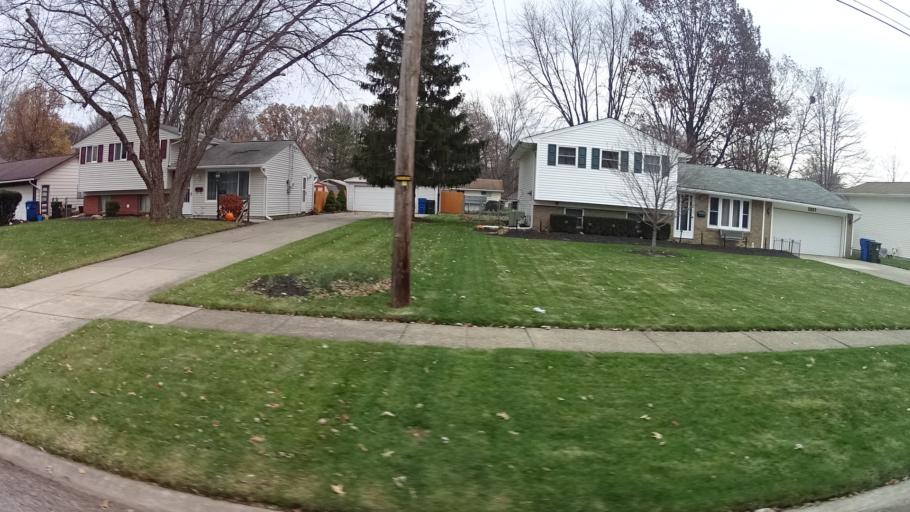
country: US
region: Ohio
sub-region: Lorain County
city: North Ridgeville
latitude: 41.4044
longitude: -82.0038
